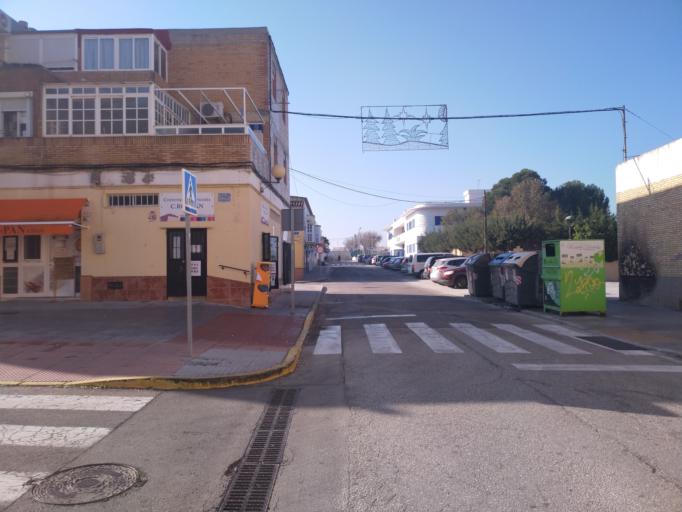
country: ES
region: Andalusia
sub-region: Provincia de Cadiz
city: San Fernando
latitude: 36.4704
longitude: -6.2012
